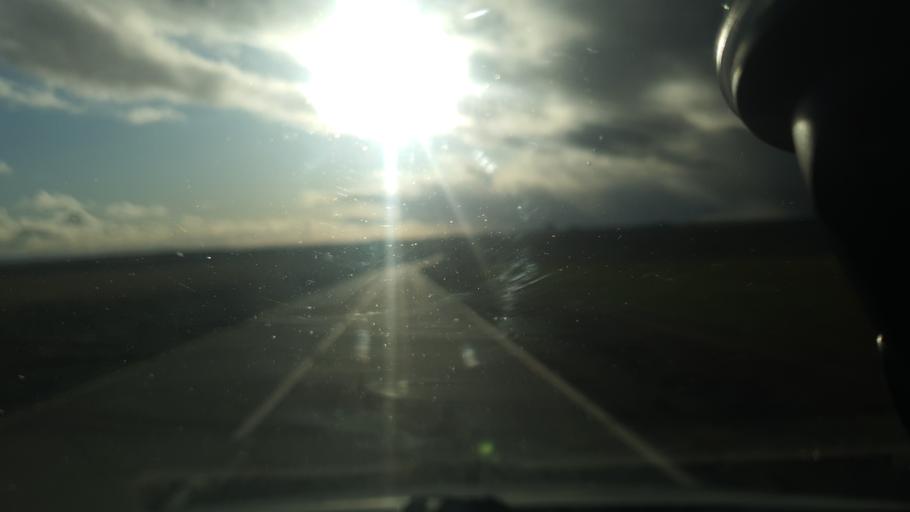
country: ES
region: Castille and Leon
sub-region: Provincia de Segovia
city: San Cristobal de la Vega
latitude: 41.1229
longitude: -4.6145
